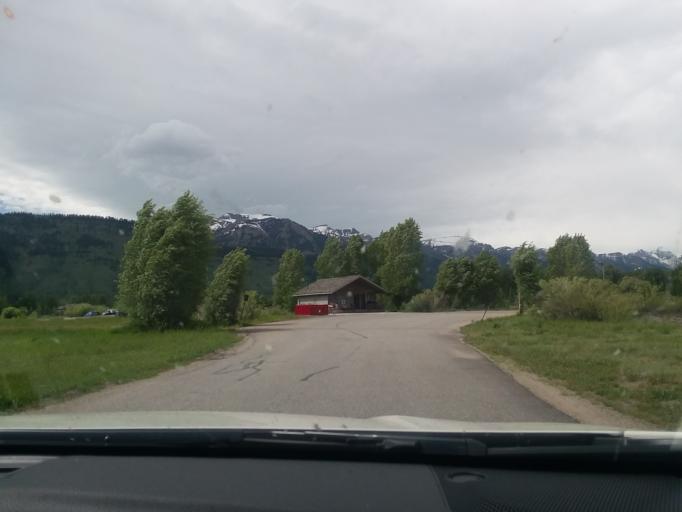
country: US
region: Wyoming
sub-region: Teton County
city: Moose Wilson Road
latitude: 43.5003
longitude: -110.8488
